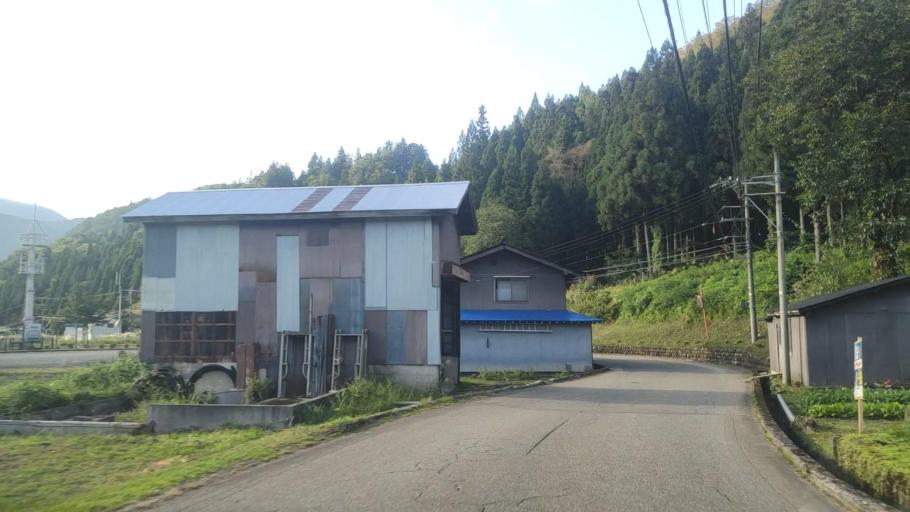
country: JP
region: Toyama
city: Yatsuomachi-higashikumisaka
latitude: 36.4791
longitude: 137.0818
